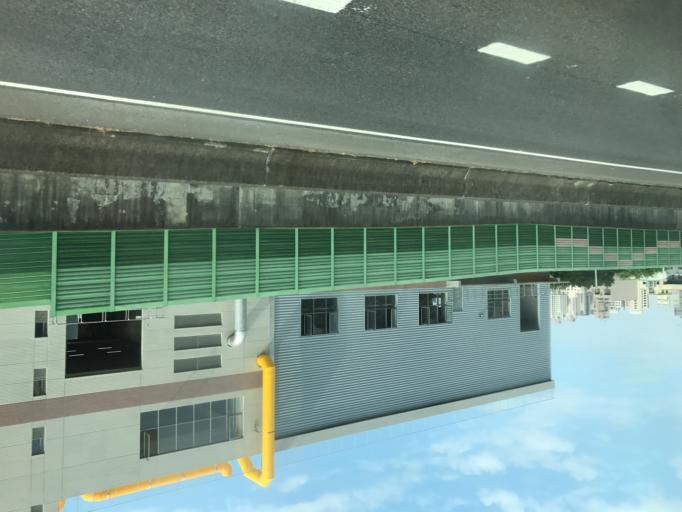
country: TW
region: Taiwan
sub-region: Hsinchu
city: Hsinchu
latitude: 24.7859
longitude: 121.0041
